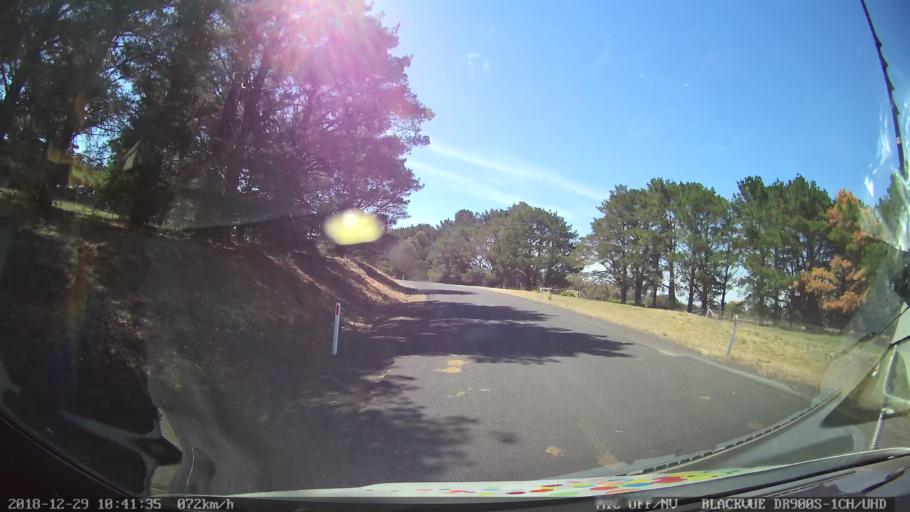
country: AU
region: New South Wales
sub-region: Palerang
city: Bungendore
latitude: -35.0269
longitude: 149.5217
